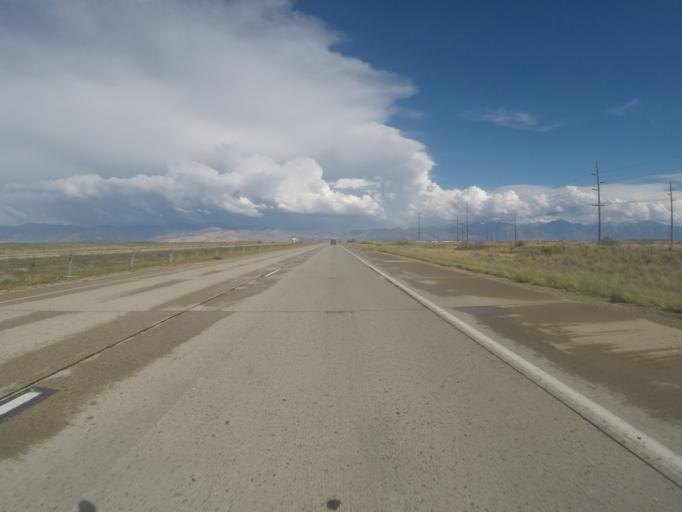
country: US
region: Utah
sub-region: Salt Lake County
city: Magna
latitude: 40.7708
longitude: -112.0979
